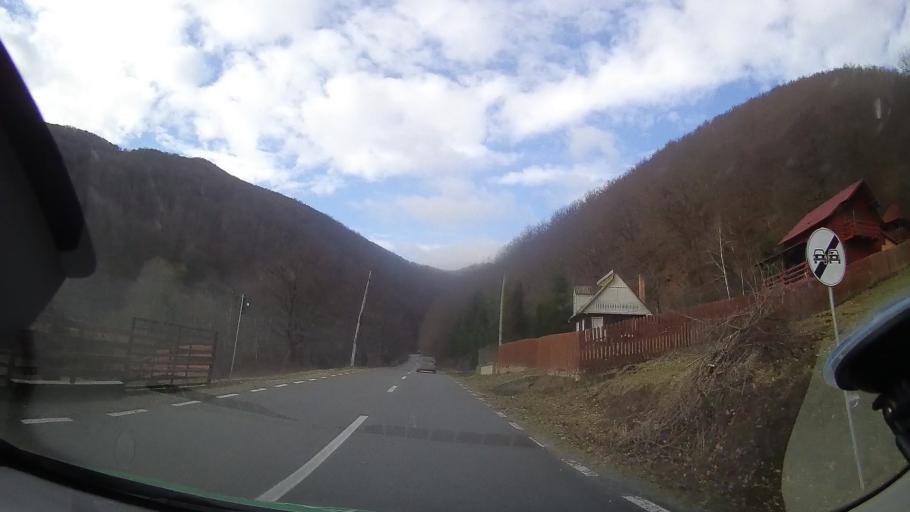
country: RO
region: Cluj
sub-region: Comuna Baisoara
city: Baisoara
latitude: 46.6122
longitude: 23.4114
